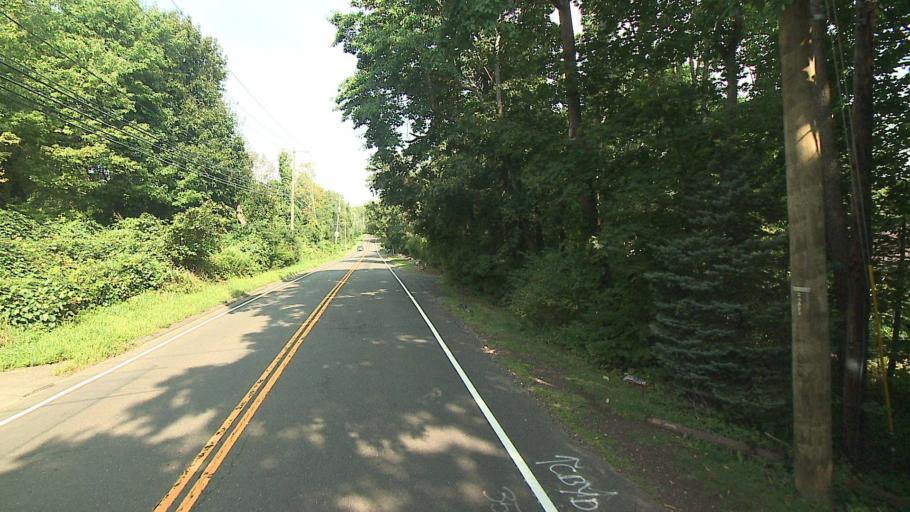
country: US
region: Connecticut
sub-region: Fairfield County
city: Georgetown
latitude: 41.2283
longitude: -73.4008
